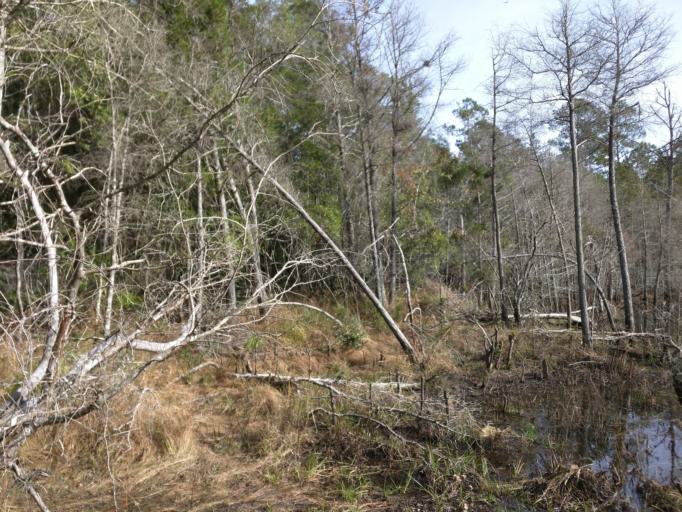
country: US
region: Florida
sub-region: Escambia County
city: Cantonment
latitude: 30.5446
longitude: -87.4308
